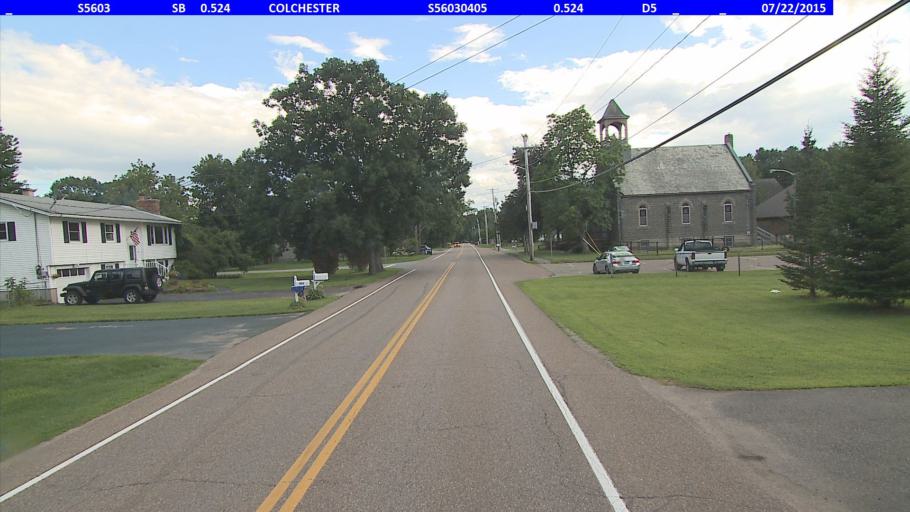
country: US
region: Vermont
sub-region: Chittenden County
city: Burlington
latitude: 44.5455
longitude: -73.2501
